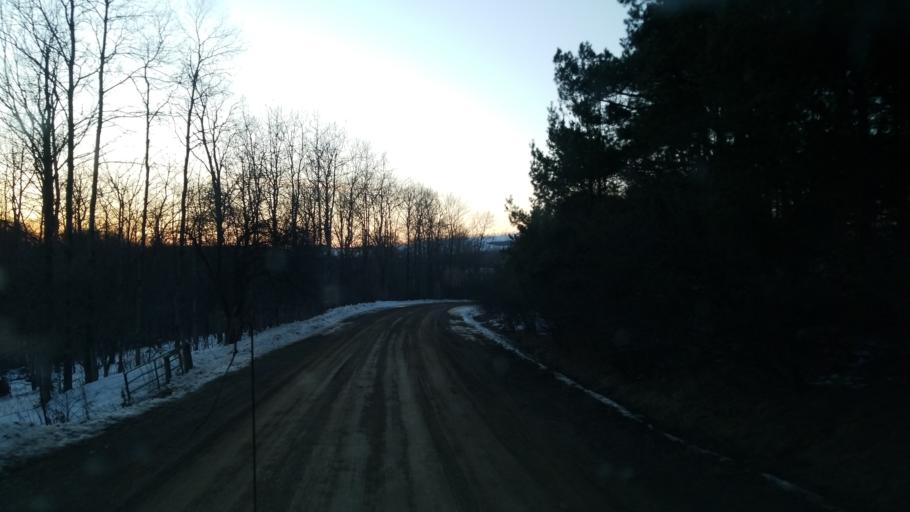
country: US
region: New York
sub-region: Allegany County
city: Andover
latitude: 42.0086
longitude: -77.7542
